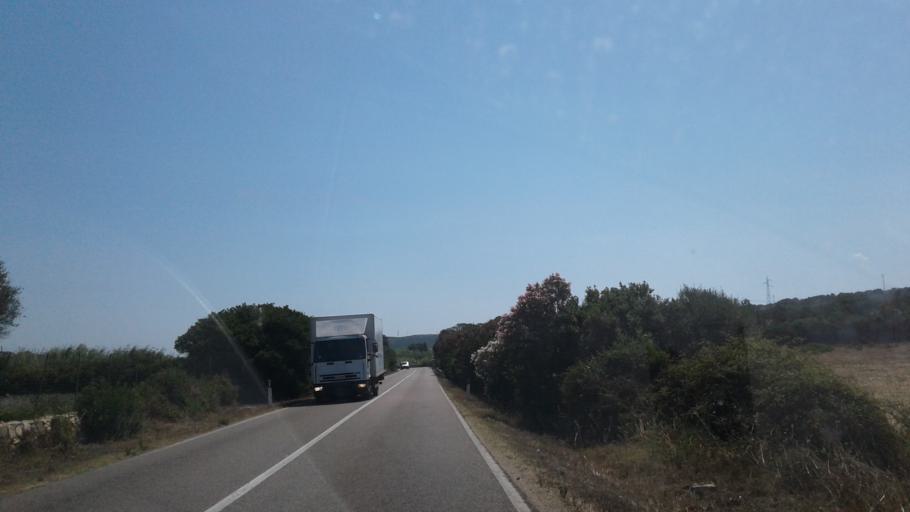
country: IT
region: Sardinia
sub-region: Provincia di Olbia-Tempio
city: Palau
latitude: 41.1710
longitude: 9.3500
